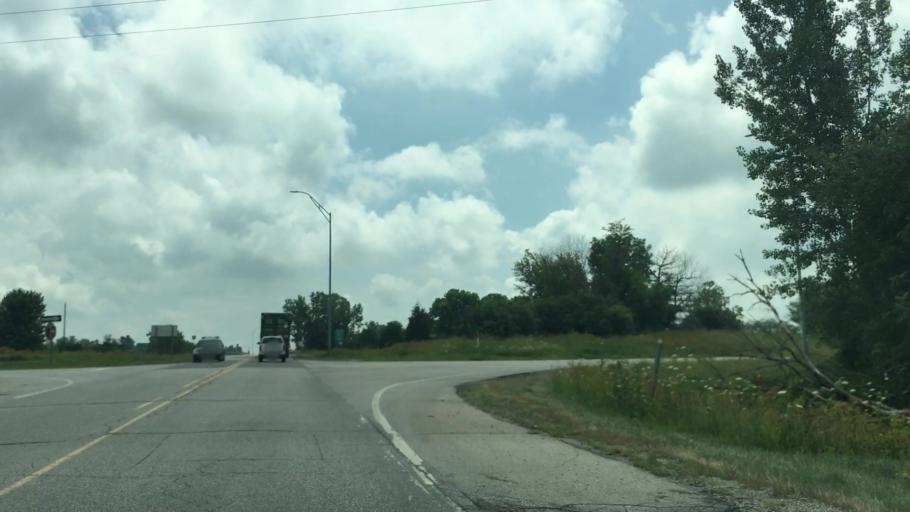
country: US
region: Iowa
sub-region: Johnson County
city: Tiffin
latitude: 41.6958
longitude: -91.6666
